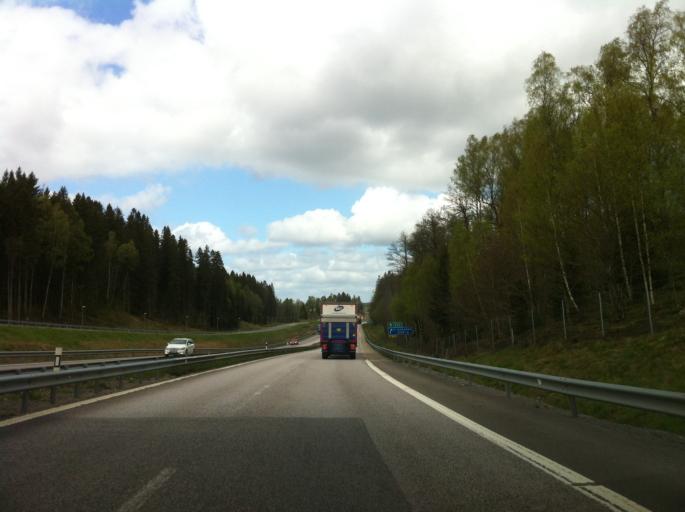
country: SE
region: Vaestra Goetaland
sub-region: Alingsas Kommun
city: Ingared
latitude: 57.8826
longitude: 12.4915
